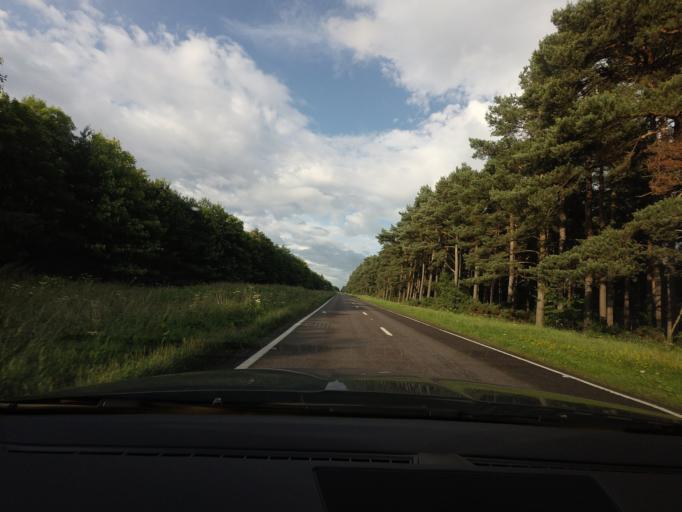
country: GB
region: Scotland
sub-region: Highland
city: Nairn
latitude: 57.5679
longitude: -3.9421
